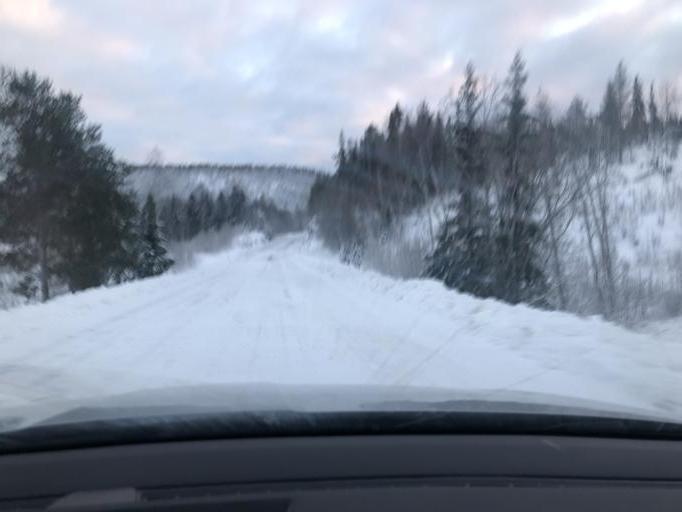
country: SE
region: Vaesternorrland
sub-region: Kramfors Kommun
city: Nordingra
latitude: 62.9870
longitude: 18.2576
